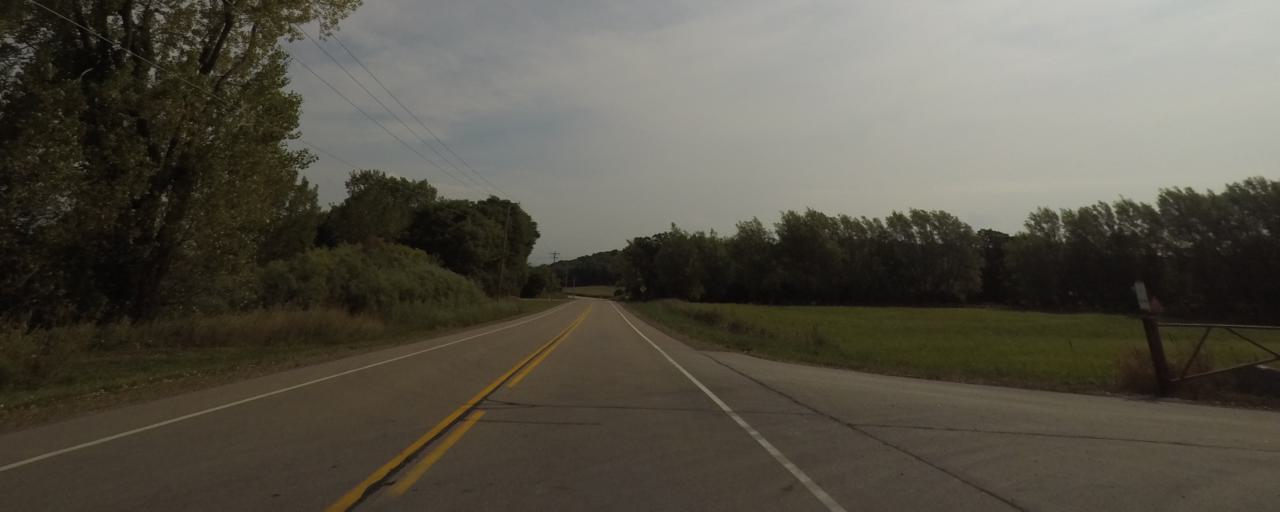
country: US
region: Wisconsin
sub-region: Jefferson County
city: Fort Atkinson
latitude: 42.9761
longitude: -88.8874
